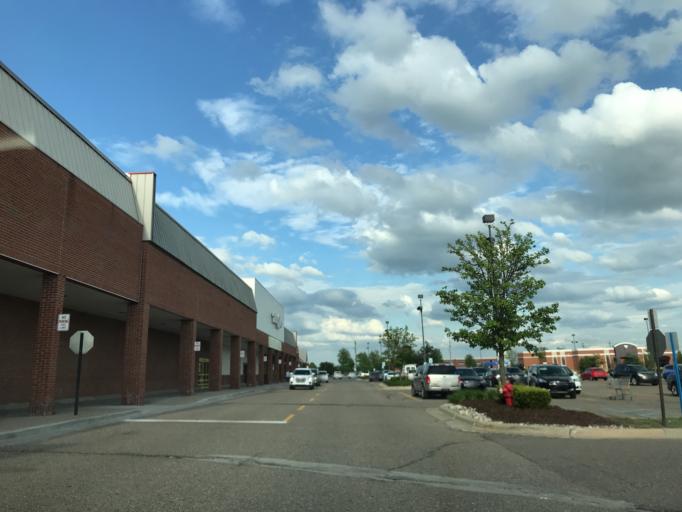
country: US
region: Michigan
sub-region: Oakland County
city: Novi
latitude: 42.4944
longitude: -83.4790
